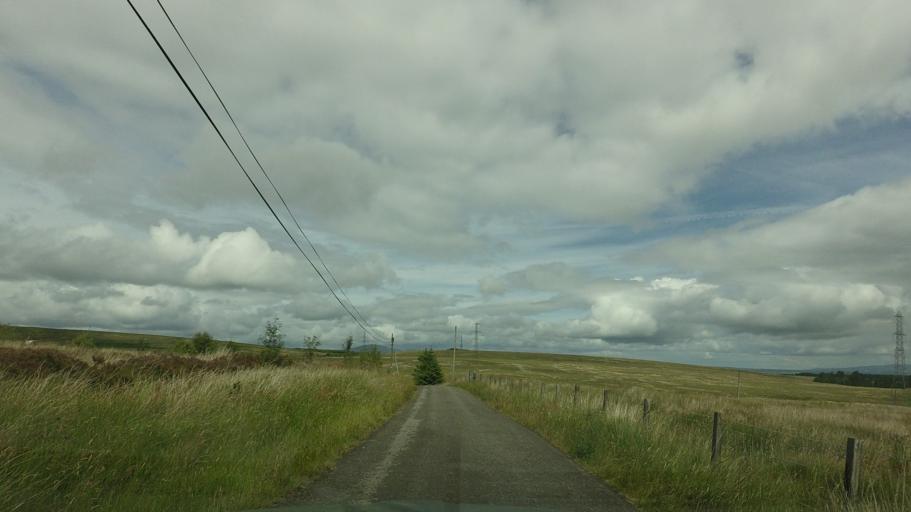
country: GB
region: Scotland
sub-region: Stirling
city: Killearn
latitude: 56.0901
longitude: -4.4335
